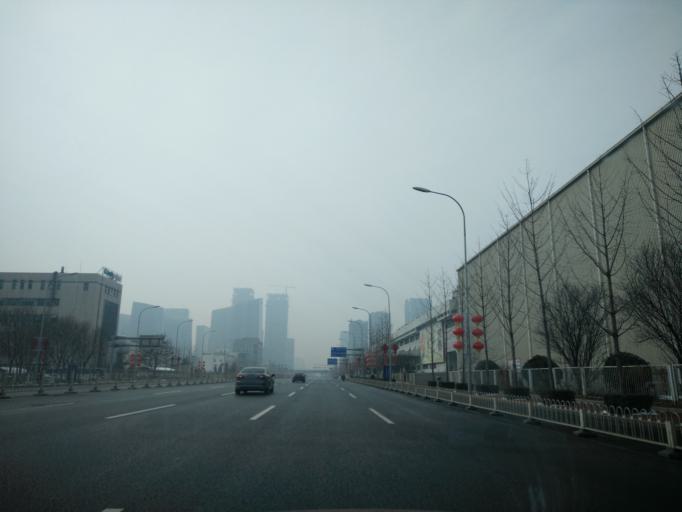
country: CN
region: Beijing
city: Jiugong
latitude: 39.7967
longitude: 116.5140
